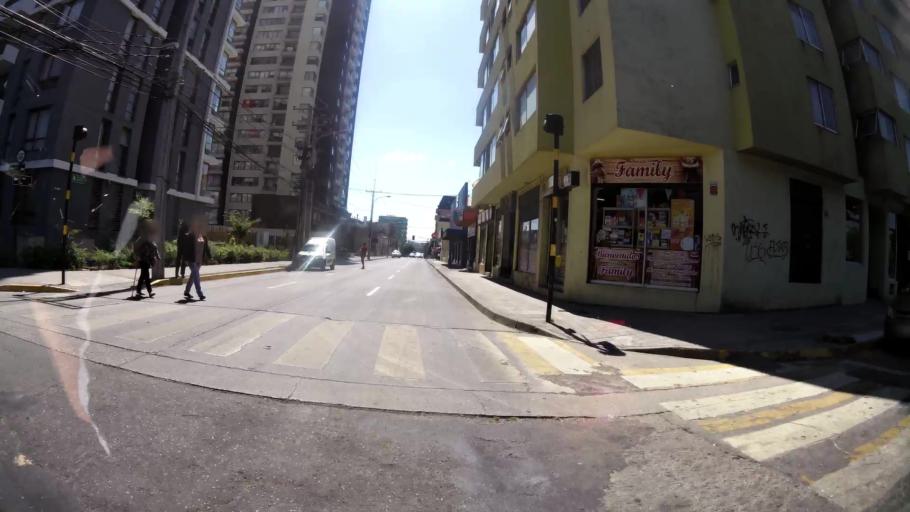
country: CL
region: Biobio
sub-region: Provincia de Concepcion
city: Concepcion
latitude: -36.8223
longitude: -73.0557
